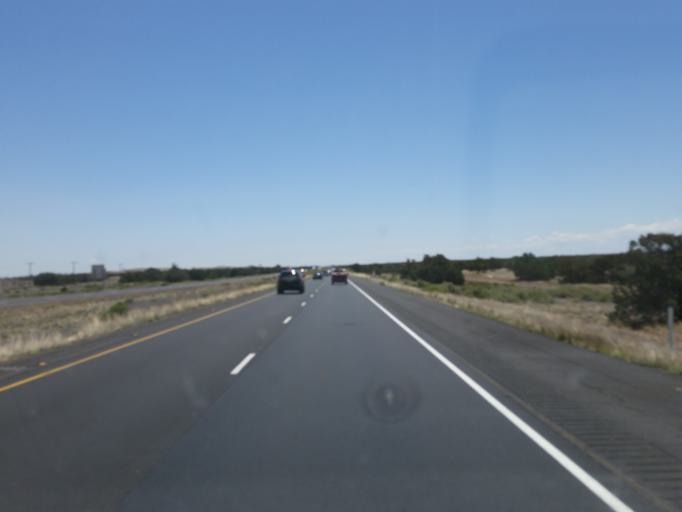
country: US
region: Arizona
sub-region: Coconino County
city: Flagstaff
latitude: 35.1943
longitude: -111.3892
